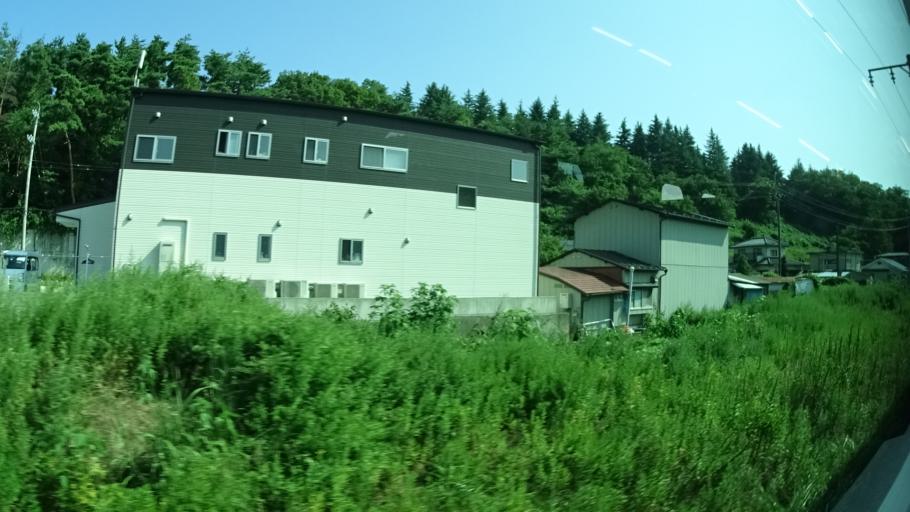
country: JP
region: Miyagi
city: Shiogama
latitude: 38.3342
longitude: 141.0306
